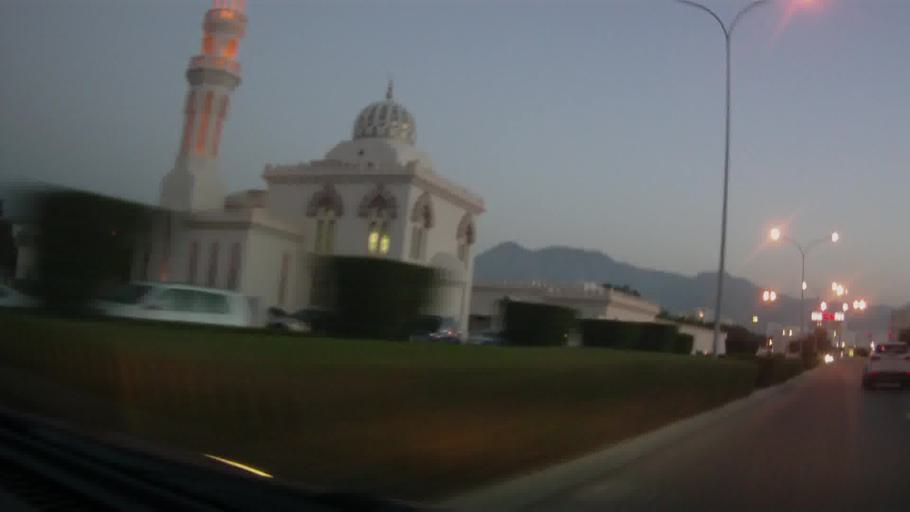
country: OM
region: Muhafazat Masqat
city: Bawshar
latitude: 23.6024
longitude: 58.4417
